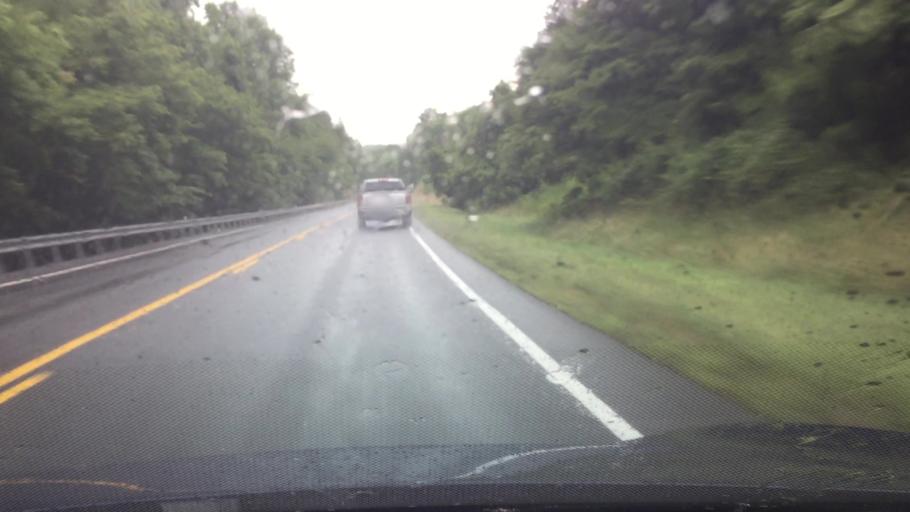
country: US
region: Virginia
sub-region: City of Bedford
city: Bedford
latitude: 37.3561
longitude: -79.4659
